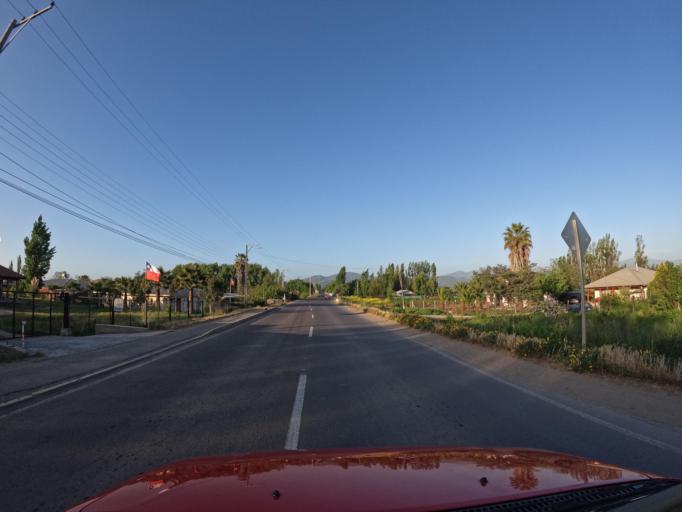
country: CL
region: O'Higgins
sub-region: Provincia de Cachapoal
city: San Vicente
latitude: -34.3100
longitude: -71.3829
